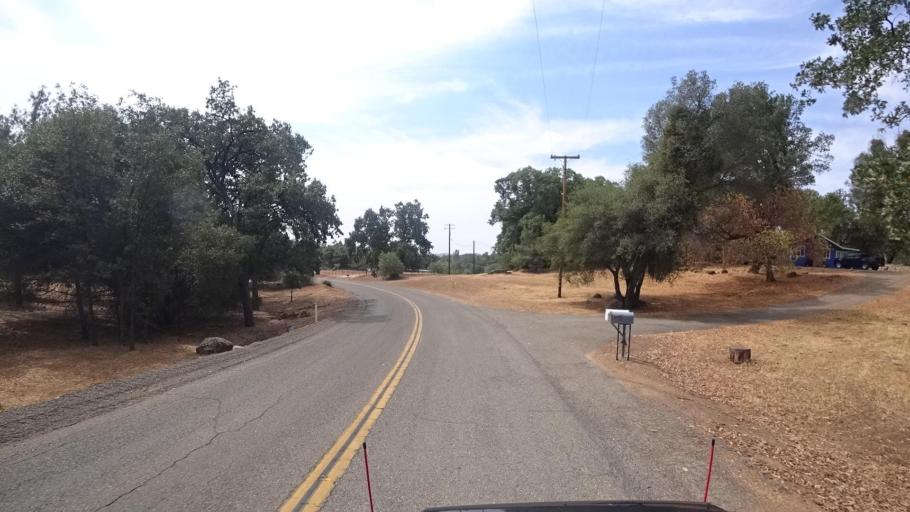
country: US
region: California
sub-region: Mariposa County
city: Midpines
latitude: 37.5110
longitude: -119.9007
